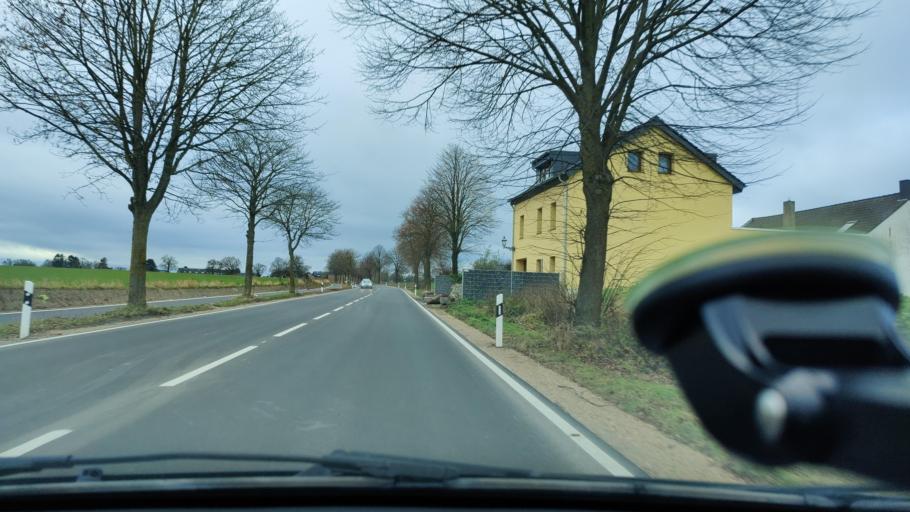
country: DE
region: North Rhine-Westphalia
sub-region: Regierungsbezirk Koln
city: Alsdorf
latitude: 50.8451
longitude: 6.1927
